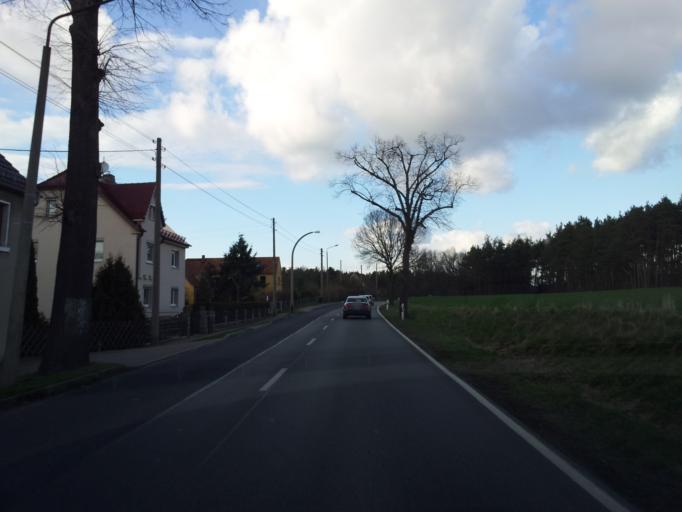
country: DE
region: Saxony
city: Konigsbruck
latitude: 51.3000
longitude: 13.9149
